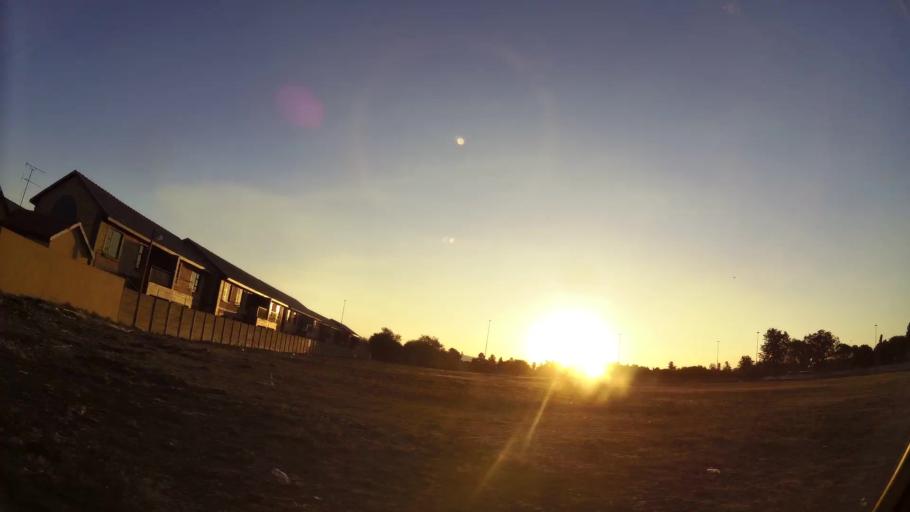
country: ZA
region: Gauteng
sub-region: Ekurhuleni Metropolitan Municipality
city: Germiston
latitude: -26.2695
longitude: 28.1516
